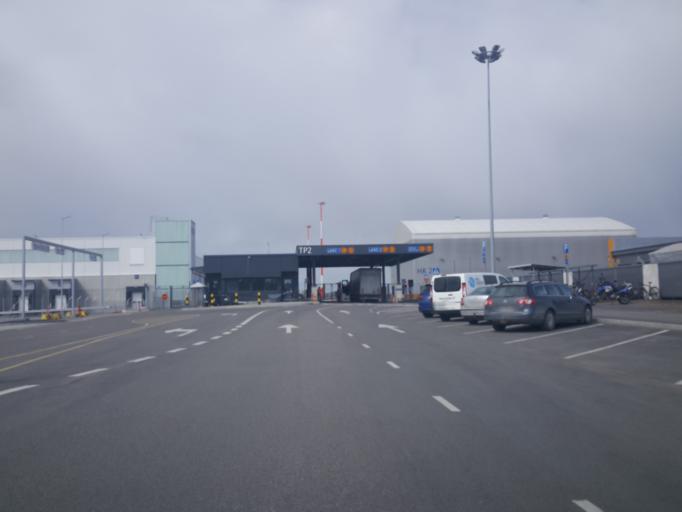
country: FI
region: Uusimaa
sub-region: Helsinki
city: Vantaa
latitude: 60.3069
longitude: 24.9567
